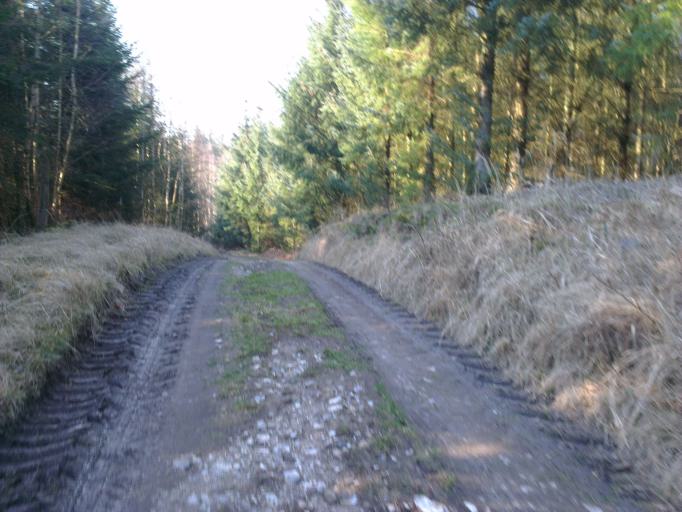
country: DK
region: Capital Region
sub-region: Frederikssund Kommune
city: Jaegerspris
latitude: 55.8981
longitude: 11.9953
